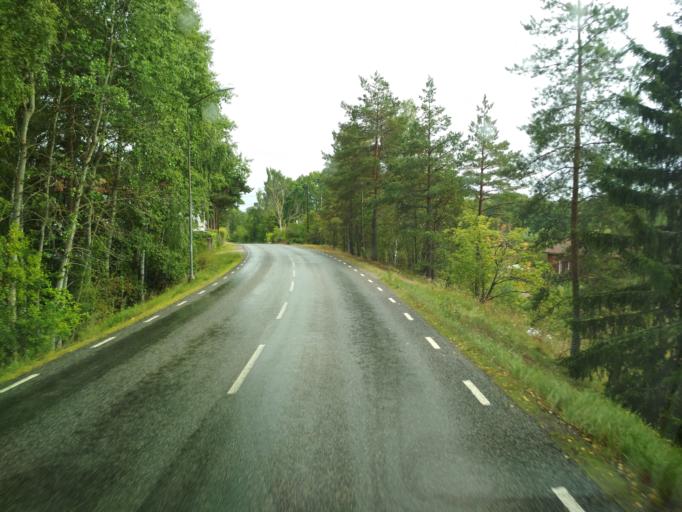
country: SE
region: Vaestmanland
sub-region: Surahammars Kommun
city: Ramnas
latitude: 59.7894
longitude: 16.1804
